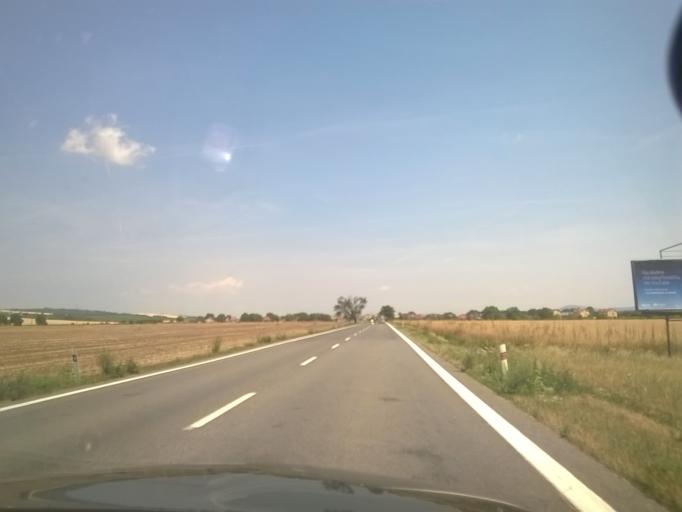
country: SK
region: Nitriansky
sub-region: Okres Nitra
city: Nitra
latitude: 48.3976
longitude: 18.0741
